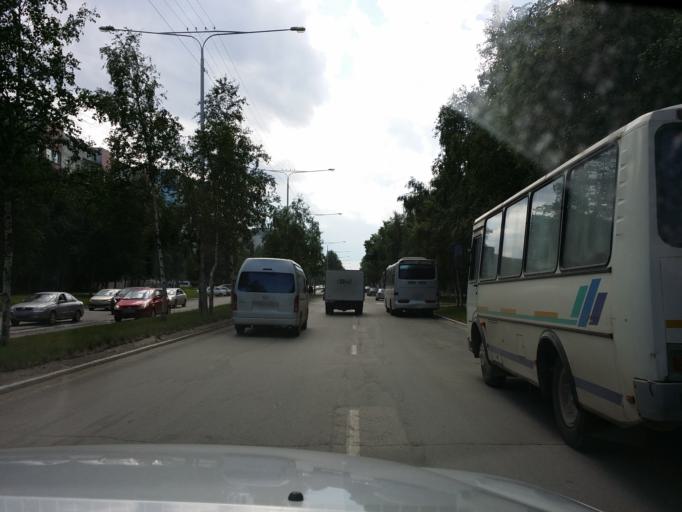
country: RU
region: Khanty-Mansiyskiy Avtonomnyy Okrug
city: Nizhnevartovsk
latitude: 60.9452
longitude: 76.5662
